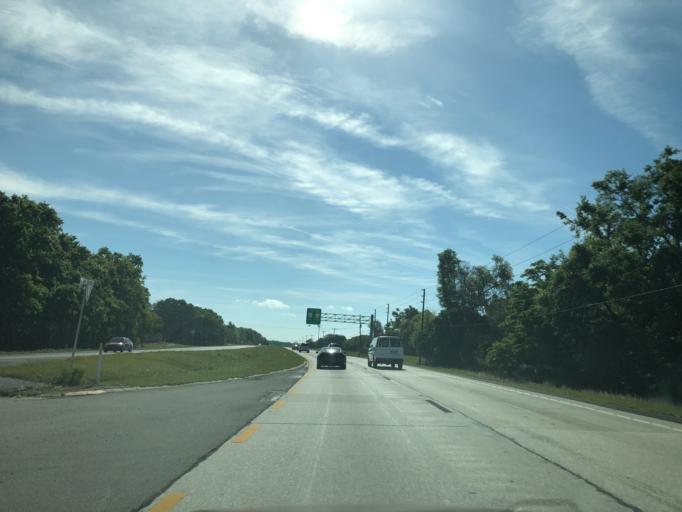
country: US
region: Florida
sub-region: Orange County
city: Zellwood
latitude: 28.7003
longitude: -81.5751
